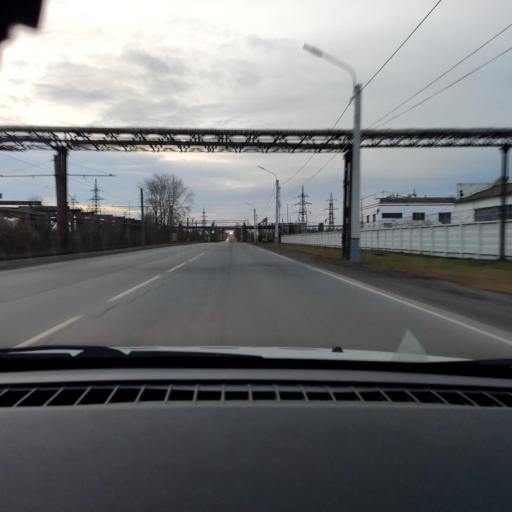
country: RU
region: Perm
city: Gamovo
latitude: 57.9155
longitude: 56.1531
